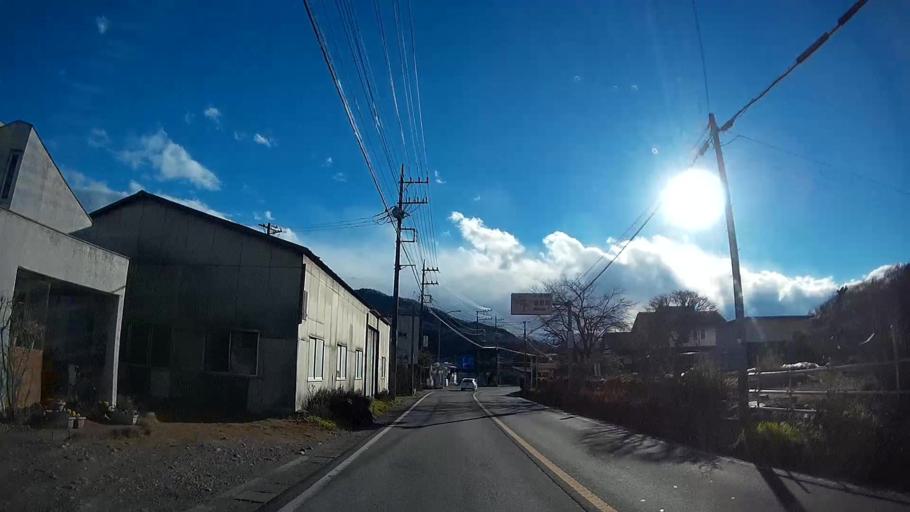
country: JP
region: Saitama
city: Yorii
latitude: 36.0857
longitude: 139.1126
